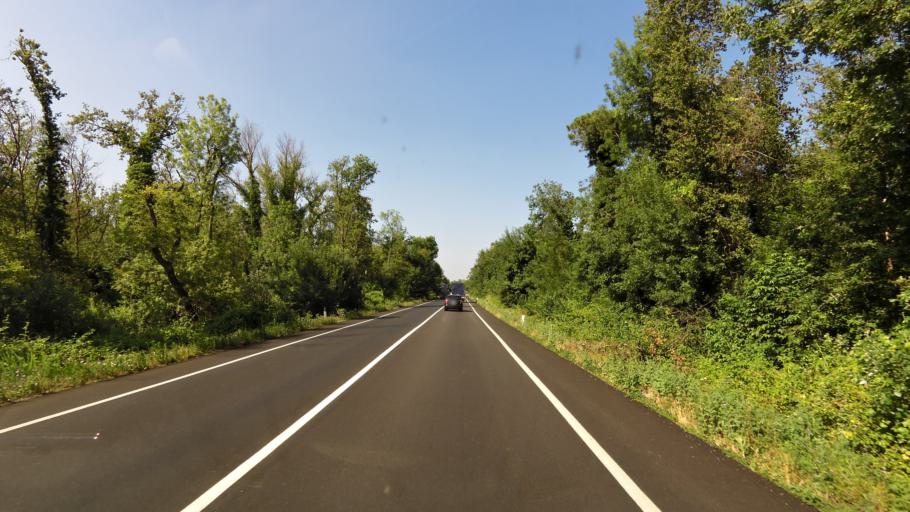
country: IT
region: Emilia-Romagna
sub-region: Provincia di Ravenna
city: Marina Romea
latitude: 44.5102
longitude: 12.2240
